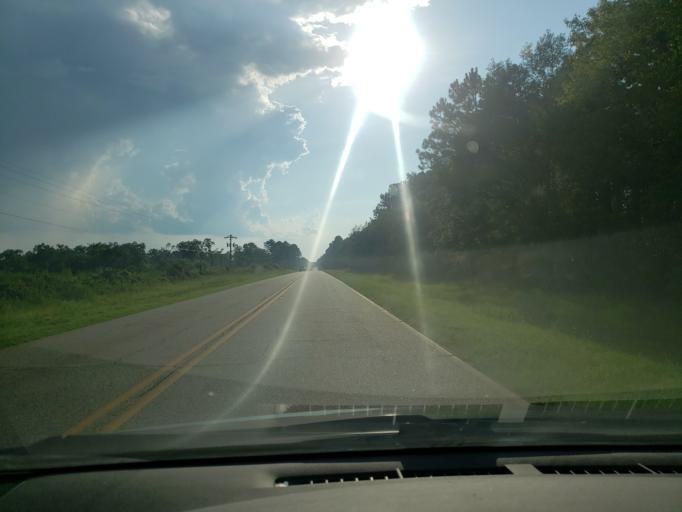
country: US
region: Georgia
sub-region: Dougherty County
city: Albany
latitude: 31.5740
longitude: -84.3119
